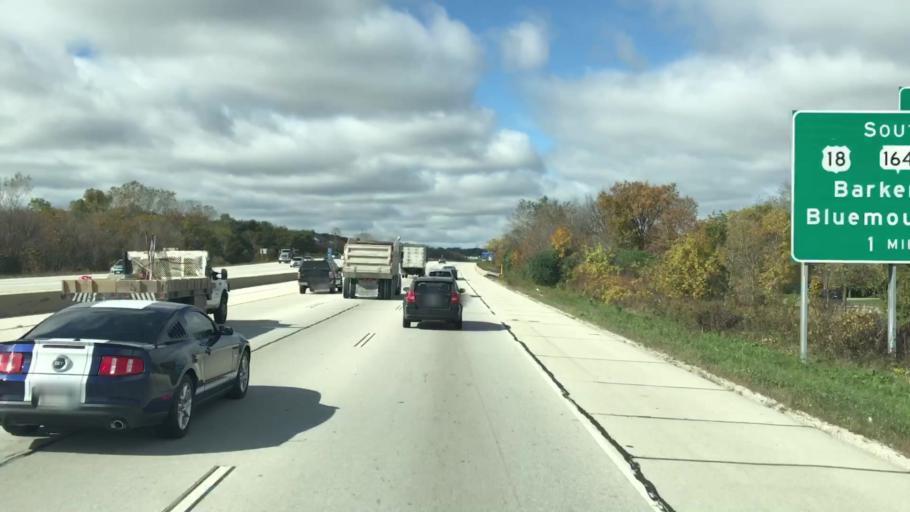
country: US
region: Wisconsin
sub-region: Waukesha County
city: Brookfield
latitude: 43.0291
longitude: -88.1419
